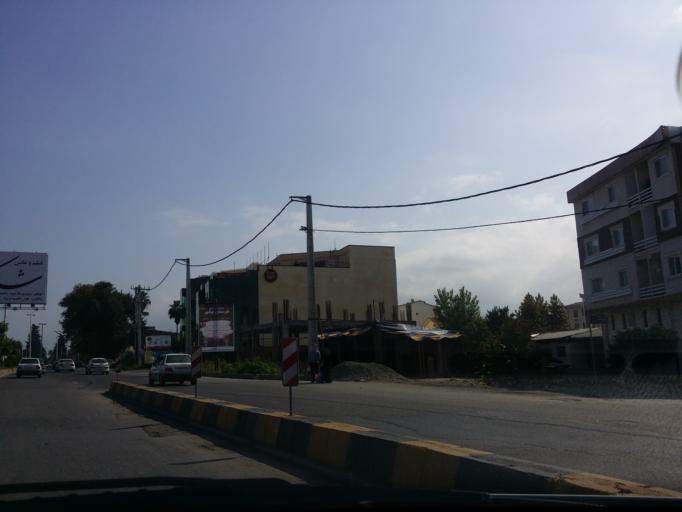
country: IR
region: Mazandaran
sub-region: Nowshahr
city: Nowshahr
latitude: 36.6569
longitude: 51.4851
